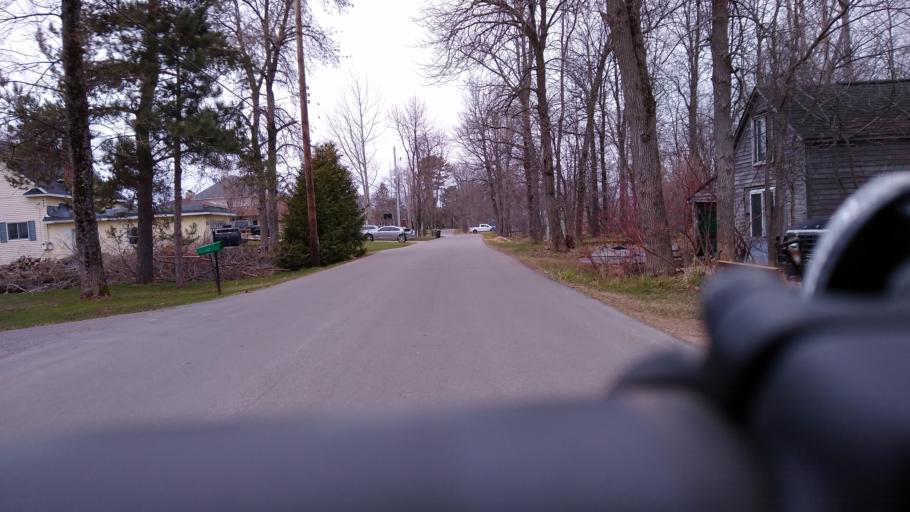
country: US
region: Michigan
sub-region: Delta County
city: Escanaba
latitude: 45.7039
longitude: -87.0874
